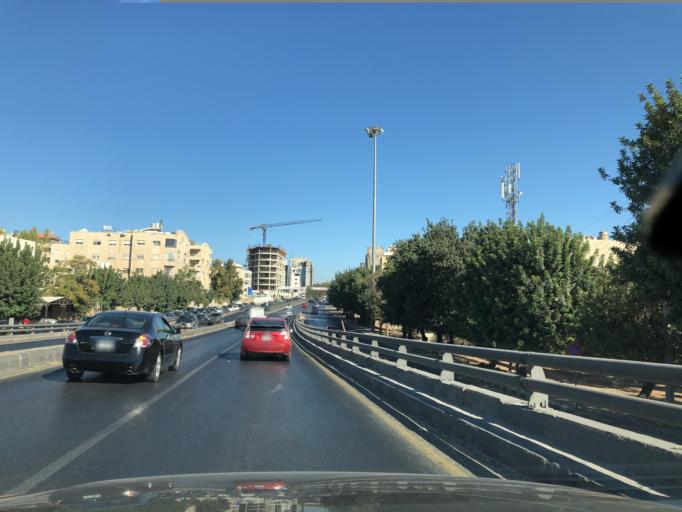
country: JO
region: Amman
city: Wadi as Sir
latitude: 31.9575
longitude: 35.8467
